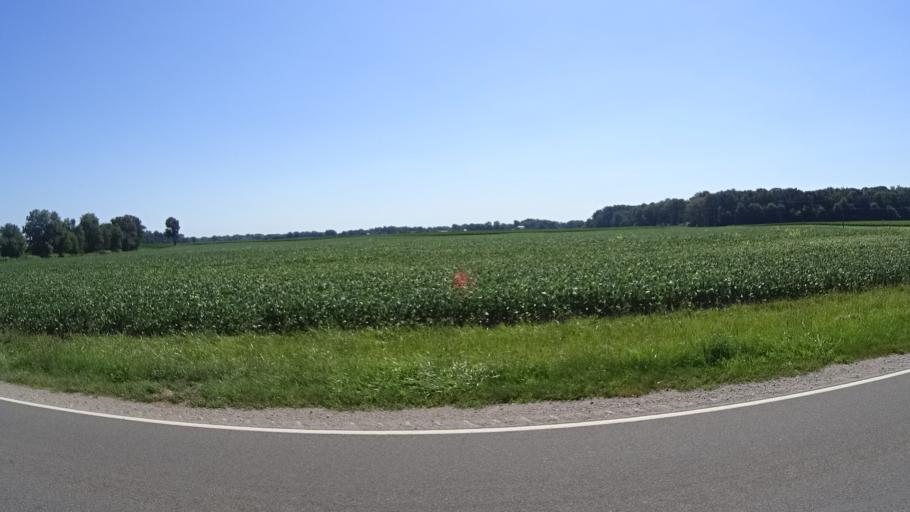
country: US
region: Ohio
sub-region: Erie County
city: Huron
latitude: 41.3782
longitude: -82.5904
